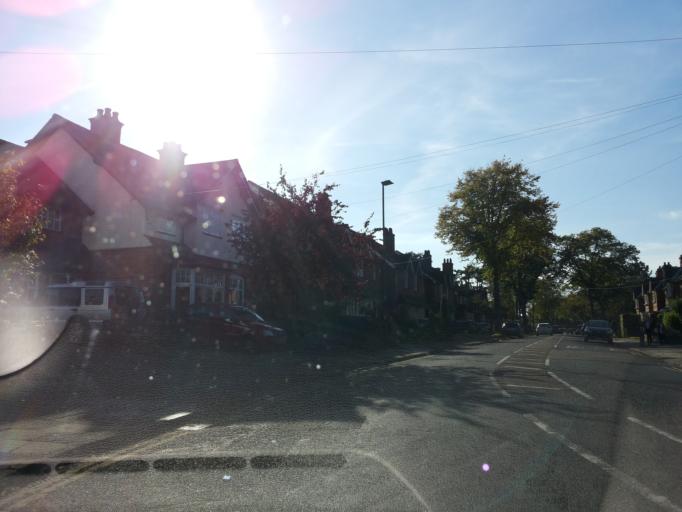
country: GB
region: England
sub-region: City and Borough of Birmingham
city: Bartley Green
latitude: 52.4251
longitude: -1.9364
